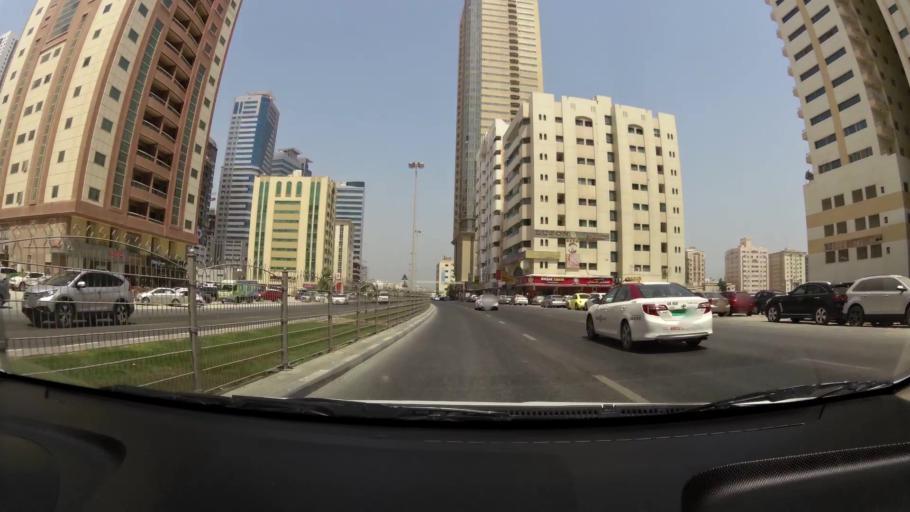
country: AE
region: Ash Shariqah
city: Sharjah
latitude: 25.3295
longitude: 55.3734
